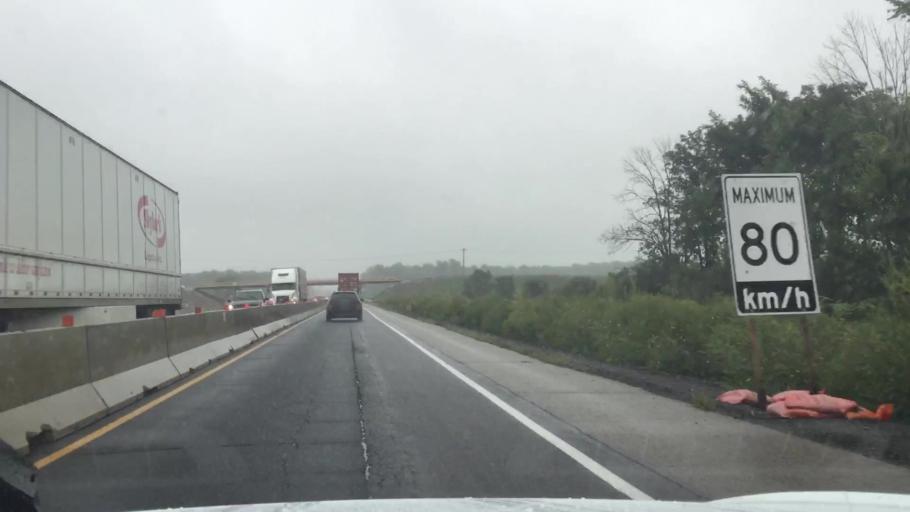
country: CA
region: Ontario
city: Delaware
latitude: 42.7928
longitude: -81.3500
